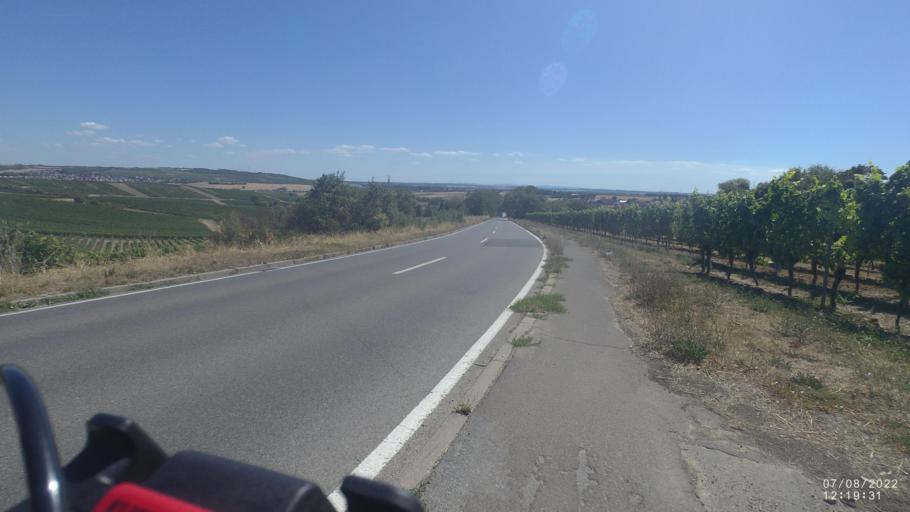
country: DE
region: Rheinland-Pfalz
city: Udenheim
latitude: 49.8687
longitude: 8.1656
